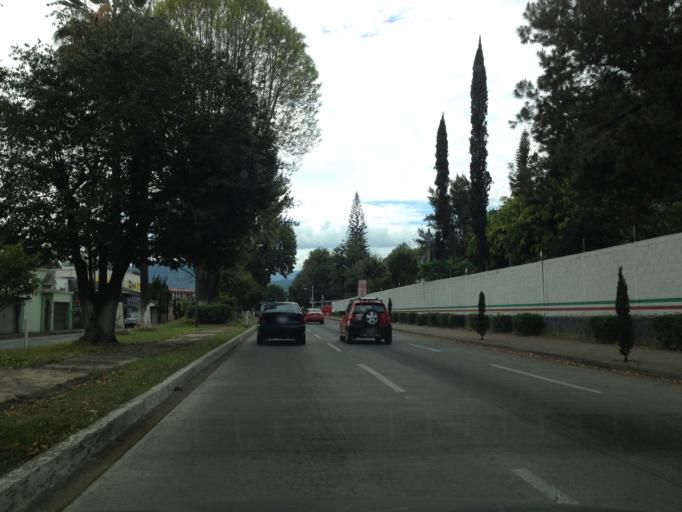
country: MX
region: Michoacan
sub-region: Uruapan
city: Uruapan
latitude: 19.4058
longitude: -102.0519
